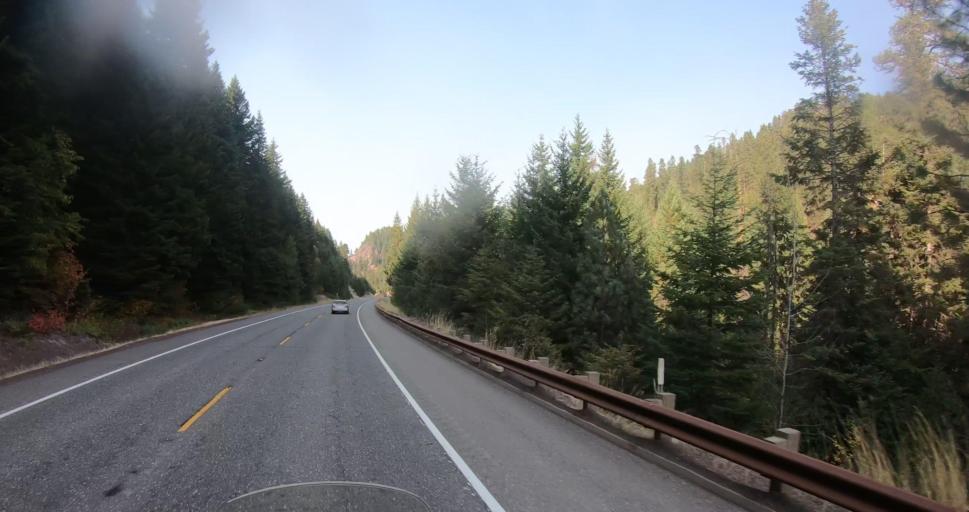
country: US
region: Oregon
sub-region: Hood River County
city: Odell
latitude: 45.4367
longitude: -121.5760
